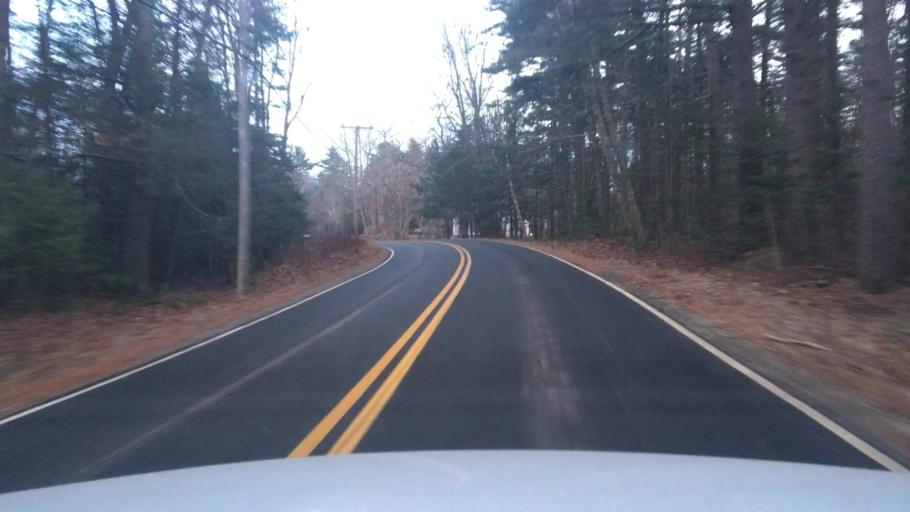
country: US
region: Maine
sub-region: Lincoln County
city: Bristol
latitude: 43.9073
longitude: -69.5262
